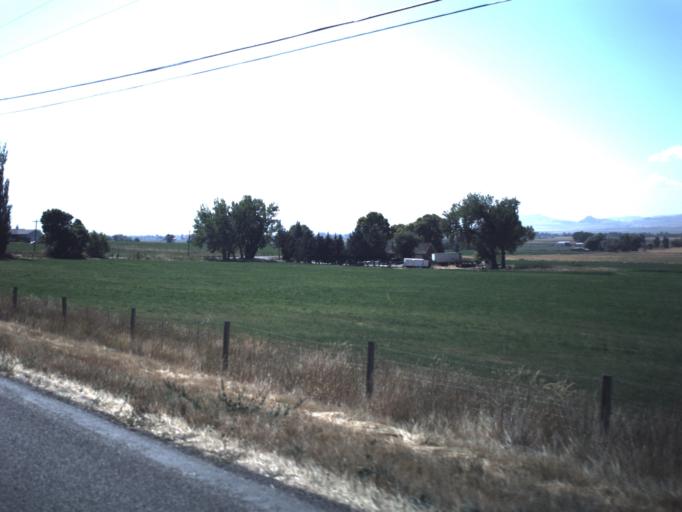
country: US
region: Utah
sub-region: Cache County
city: Smithfield
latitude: 41.8762
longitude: -111.8241
